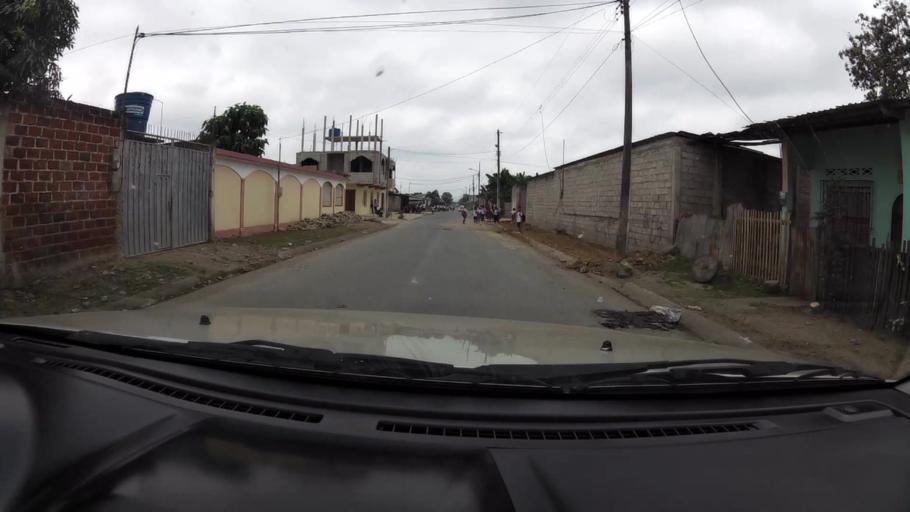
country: EC
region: El Oro
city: Pasaje
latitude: -3.2365
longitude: -79.8268
